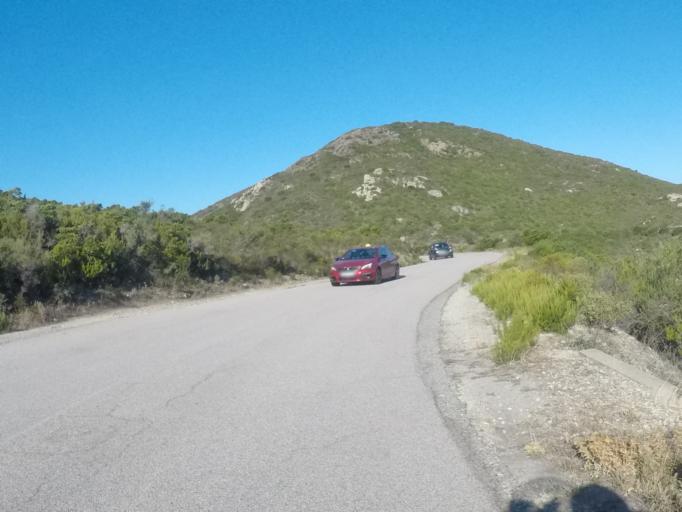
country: FR
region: Corsica
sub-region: Departement de la Haute-Corse
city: Saint-Florent
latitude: 42.6667
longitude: 9.1447
